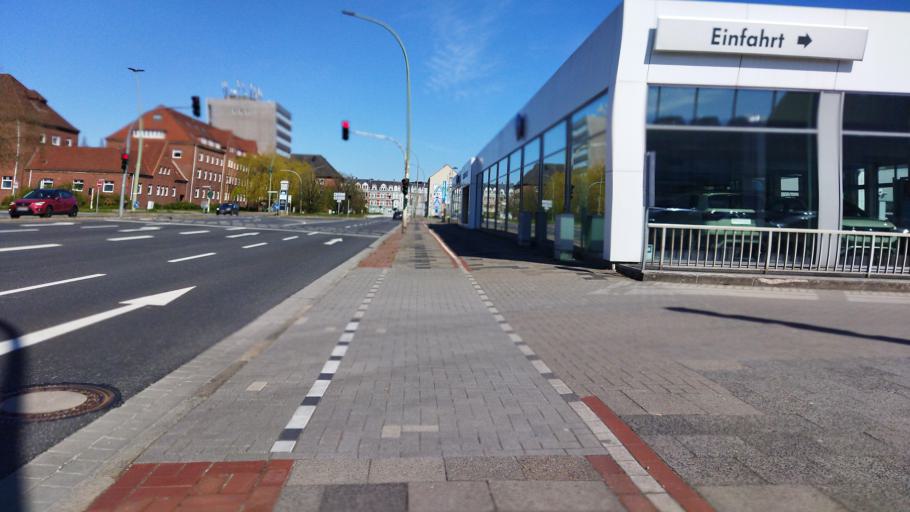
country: DE
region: Bremen
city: Bremerhaven
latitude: 53.5563
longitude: 8.5933
